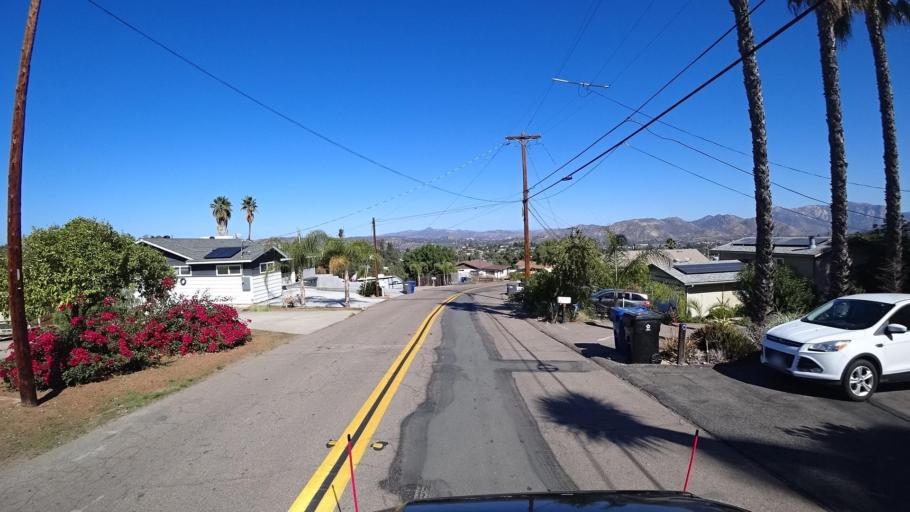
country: US
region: California
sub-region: San Diego County
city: Winter Gardens
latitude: 32.8363
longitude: -116.9386
